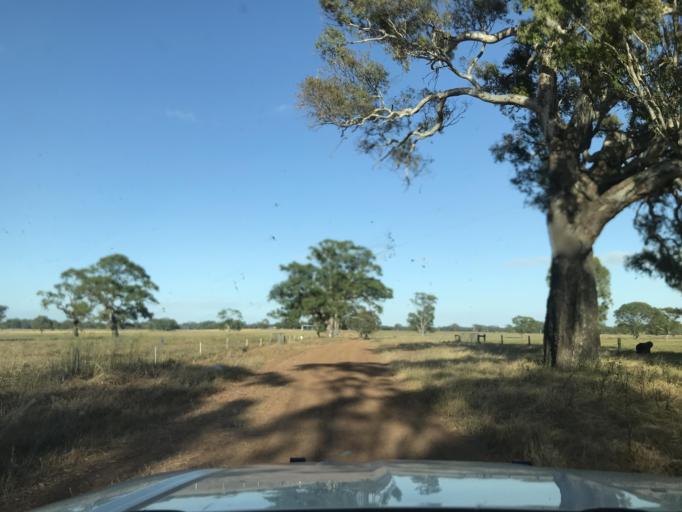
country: AU
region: South Australia
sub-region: Naracoorte and Lucindale
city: Naracoorte
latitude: -36.9558
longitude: 141.3689
